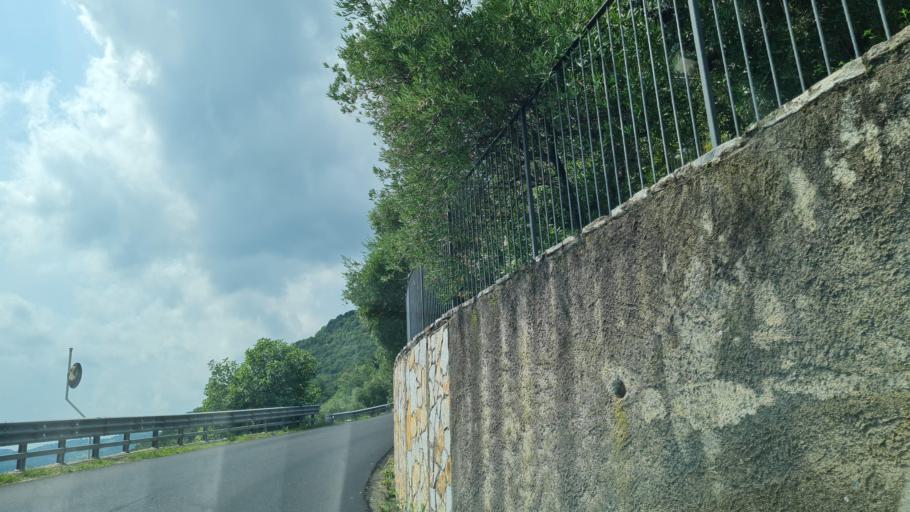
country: IT
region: Veneto
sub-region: Provincia di Vicenza
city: Marostica
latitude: 45.7813
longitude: 11.6754
